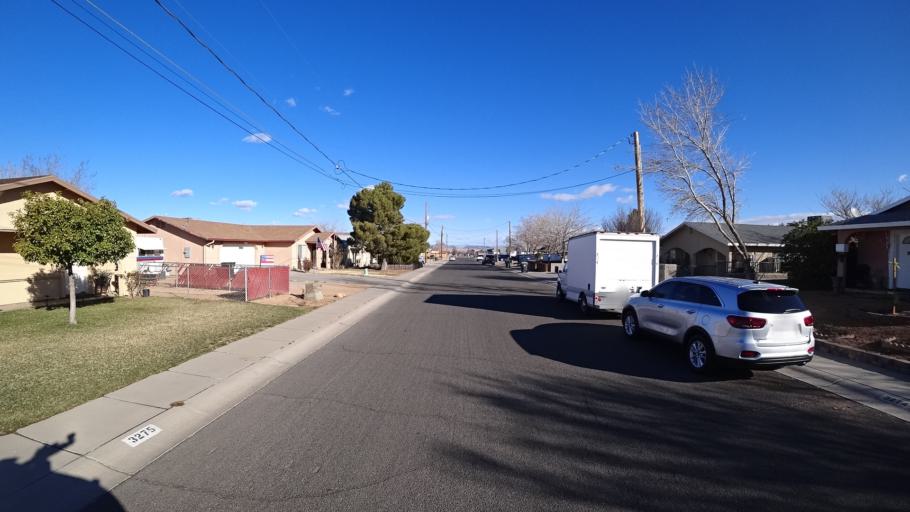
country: US
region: Arizona
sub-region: Mohave County
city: New Kingman-Butler
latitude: 35.2195
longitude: -113.9960
